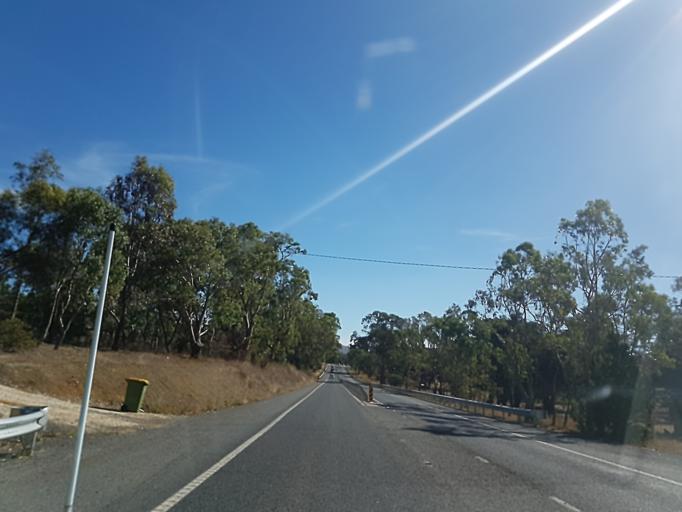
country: AU
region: Victoria
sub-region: Murrindindi
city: Alexandra
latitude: -37.2106
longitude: 145.4512
